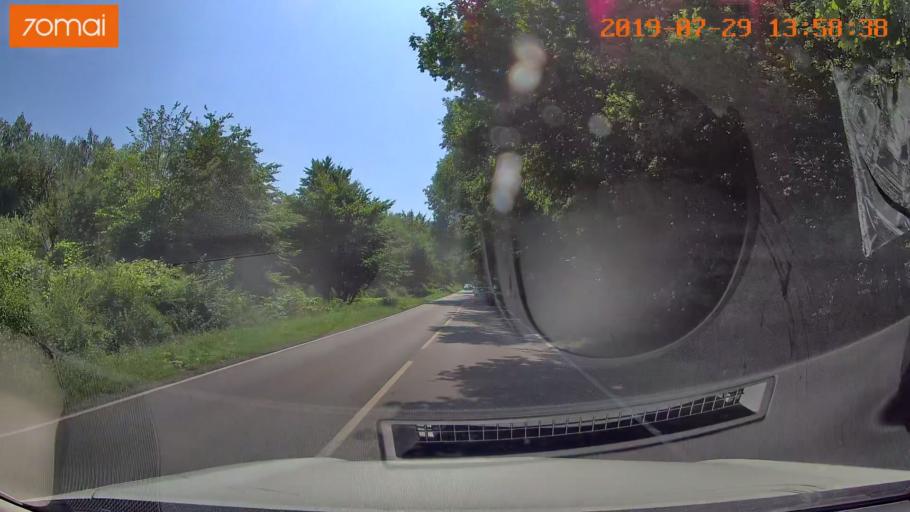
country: RU
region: Kaliningrad
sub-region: Gorod Kaliningrad
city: Baltiysk
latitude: 54.6917
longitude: 19.9359
